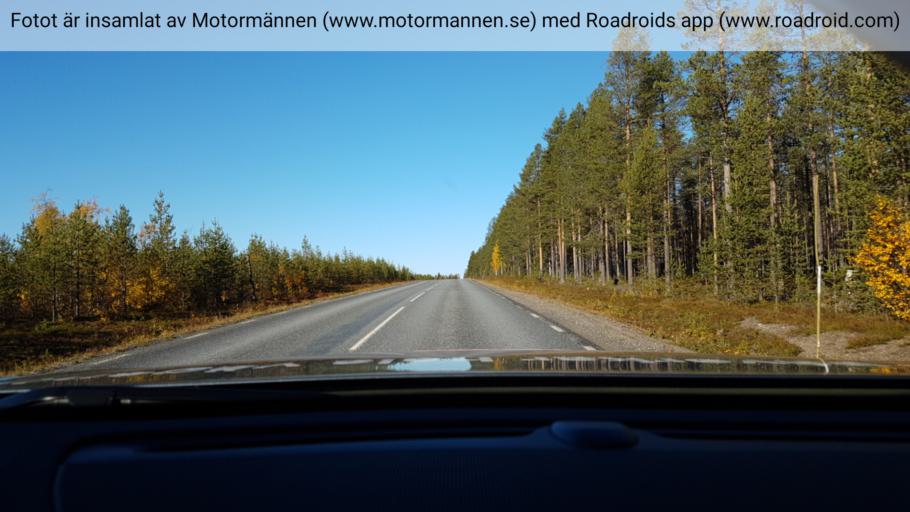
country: SE
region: Vaesterbotten
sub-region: Skelleftea Kommun
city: Langsele
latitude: 65.3831
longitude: 20.1106
